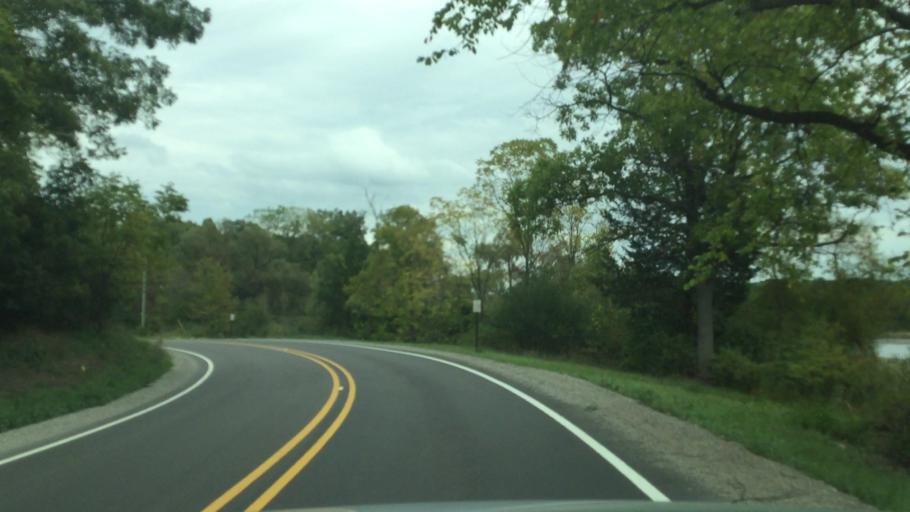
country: US
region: Michigan
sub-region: Livingston County
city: Brighton
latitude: 42.4720
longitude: -83.8254
